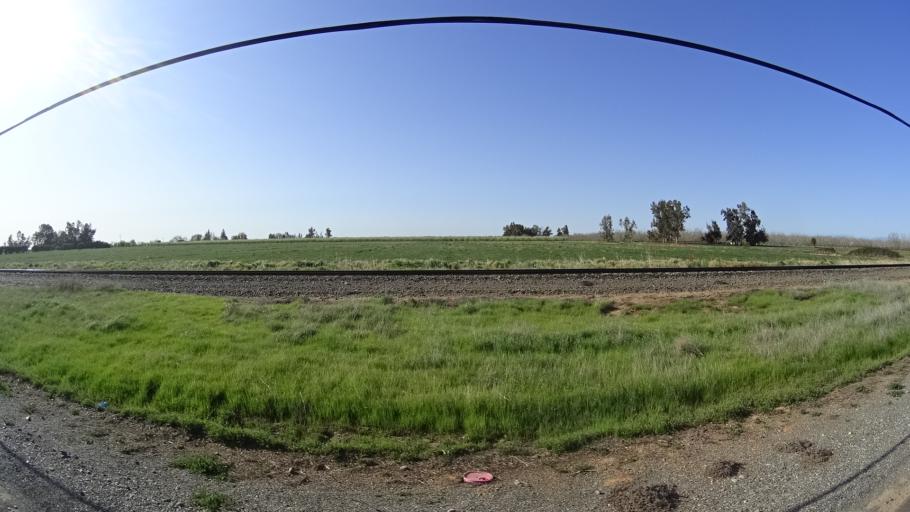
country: US
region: California
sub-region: Glenn County
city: Orland
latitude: 39.7688
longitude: -122.1262
